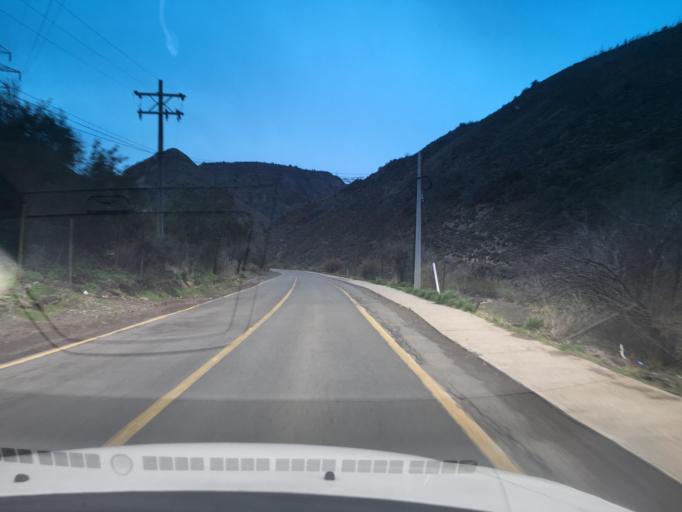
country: CL
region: Santiago Metropolitan
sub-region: Provincia de Cordillera
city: Puente Alto
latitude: -33.7364
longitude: -70.2995
